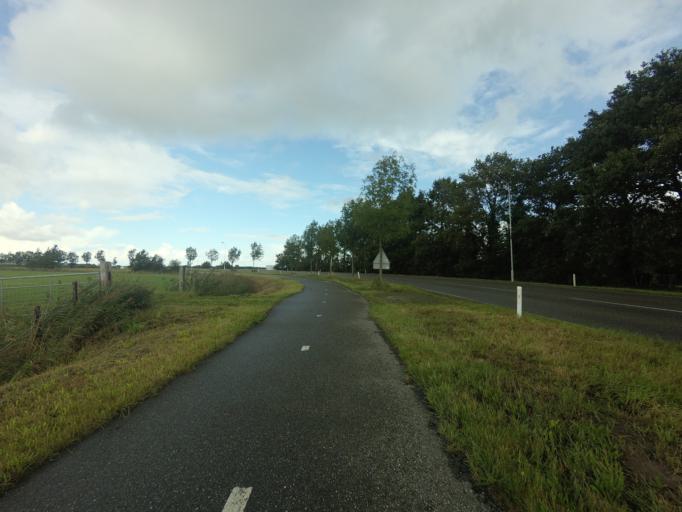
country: NL
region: Friesland
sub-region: Gemeente Tytsjerksteradiel
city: Garyp
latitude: 53.1610
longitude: 5.9490
